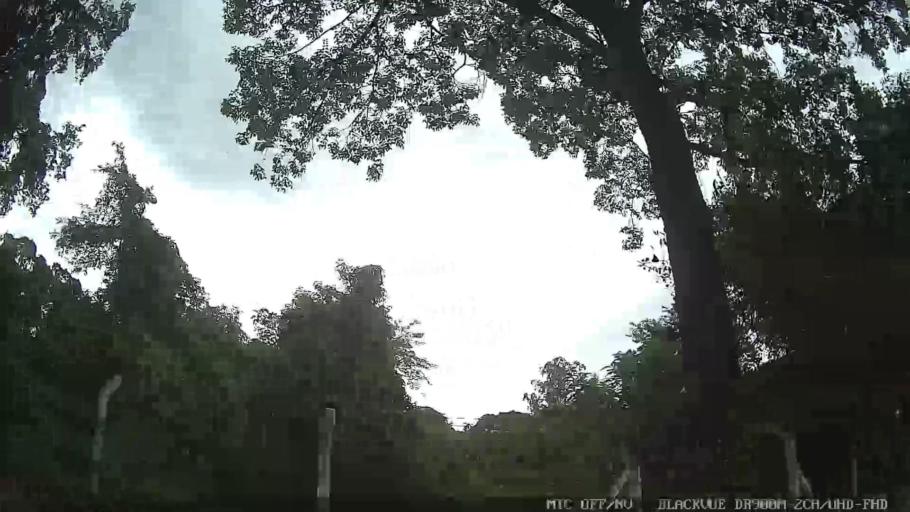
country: BR
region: Sao Paulo
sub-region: Jaguariuna
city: Jaguariuna
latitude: -22.6812
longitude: -46.9849
